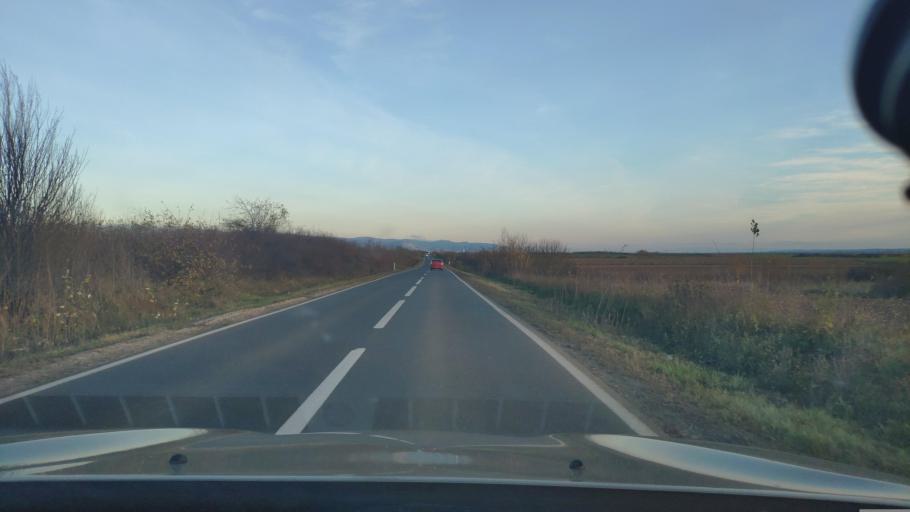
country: RO
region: Satu Mare
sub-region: Comuna Mediesu Aurit
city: Mediesu Aurit
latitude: 47.7710
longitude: 23.1415
